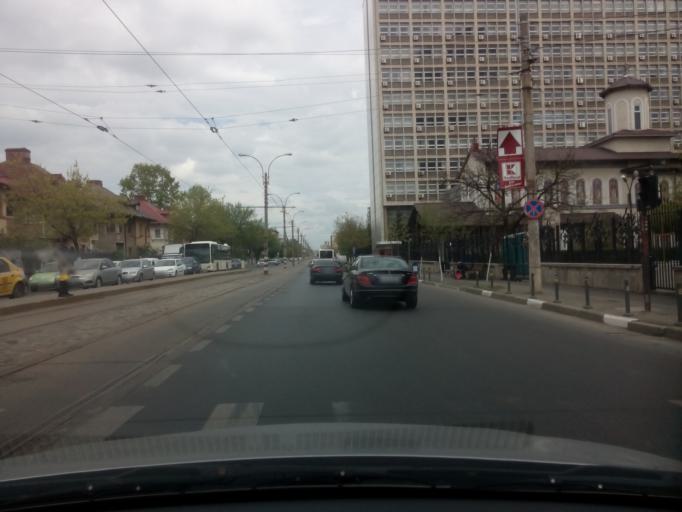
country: RO
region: Bucuresti
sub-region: Municipiul Bucuresti
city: Bucharest
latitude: 44.4572
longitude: 26.1060
